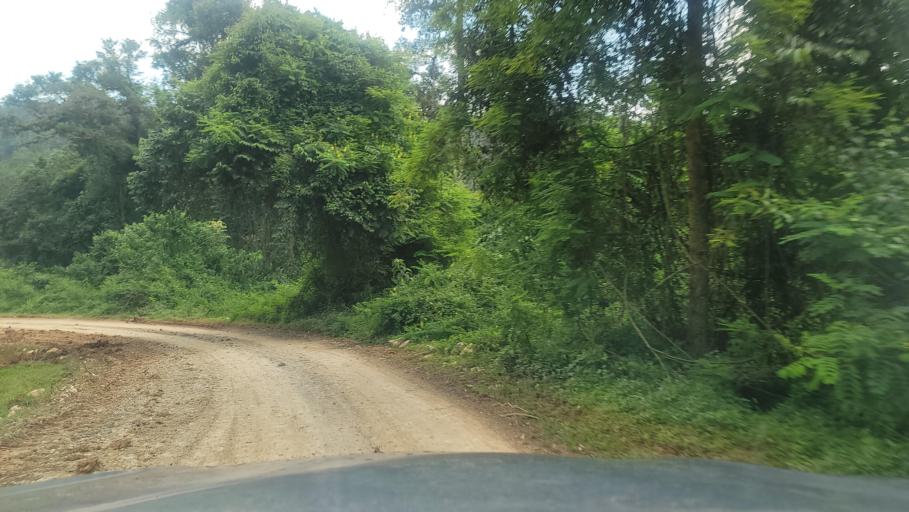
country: ET
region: Southern Nations, Nationalities, and People's Region
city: Bonga
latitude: 7.6151
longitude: 36.2051
